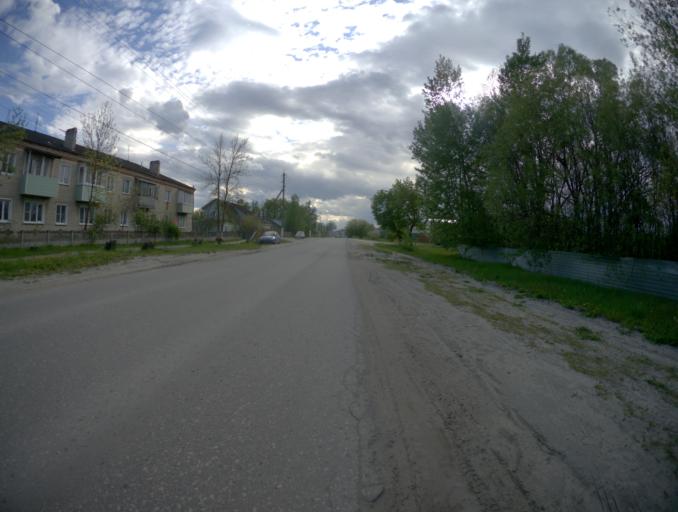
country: RU
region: Rjazan
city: Spas-Klepiki
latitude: 55.1376
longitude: 40.1869
